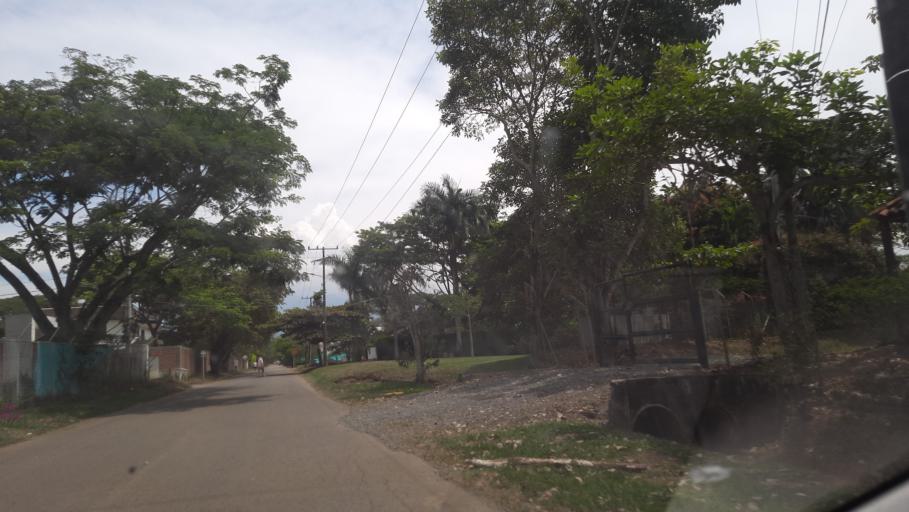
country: CO
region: Valle del Cauca
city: Jamundi
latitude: 3.2682
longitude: -76.5131
